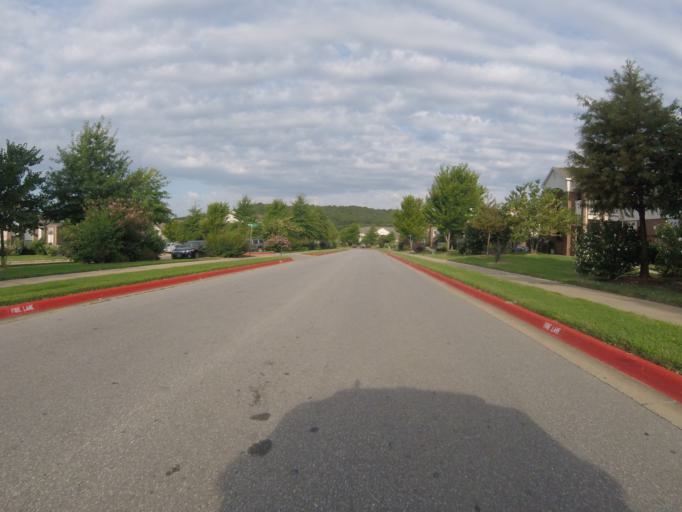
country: US
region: Arkansas
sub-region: Washington County
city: Fayetteville
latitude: 36.0599
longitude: -94.1944
